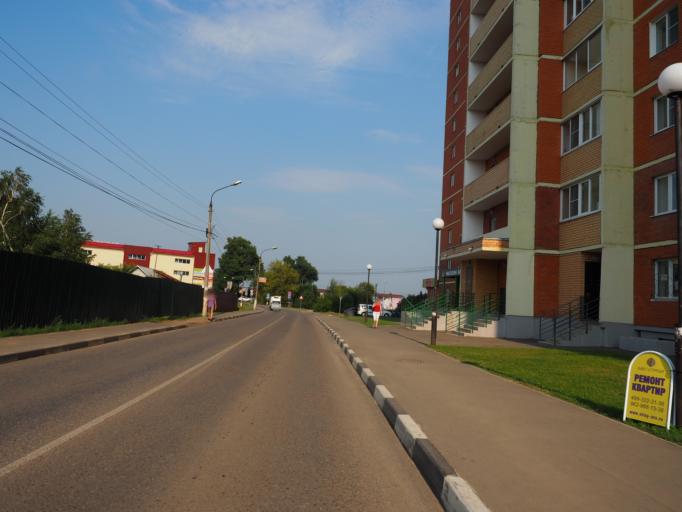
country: RU
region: Moskovskaya
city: Oktyabr'skiy
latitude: 55.6118
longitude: 37.9708
